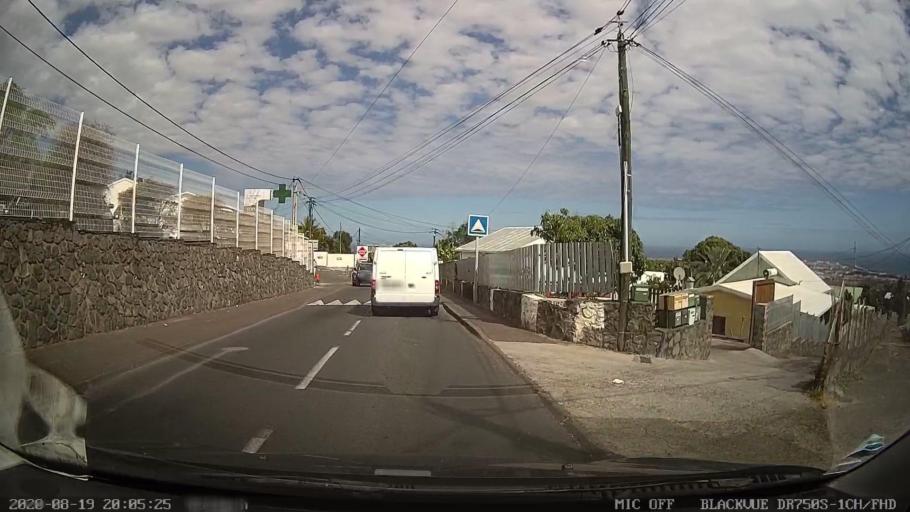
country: RE
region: Reunion
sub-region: Reunion
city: La Possession
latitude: -20.9543
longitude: 55.3395
